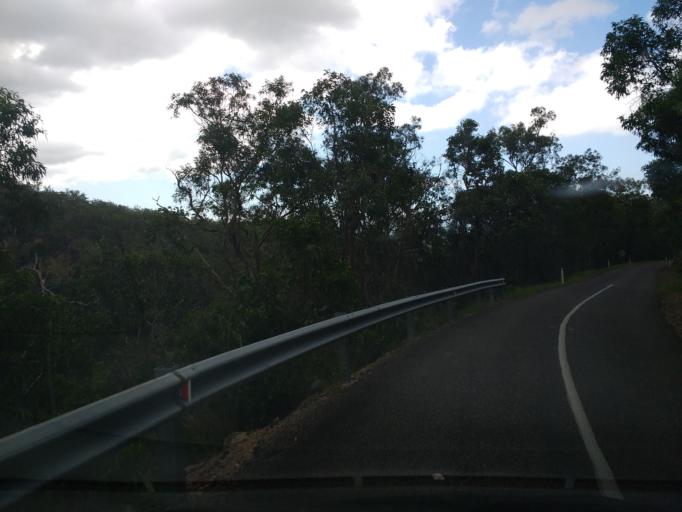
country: AU
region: Queensland
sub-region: Hinchinbrook
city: Ingham
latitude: -19.0130
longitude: 146.2712
